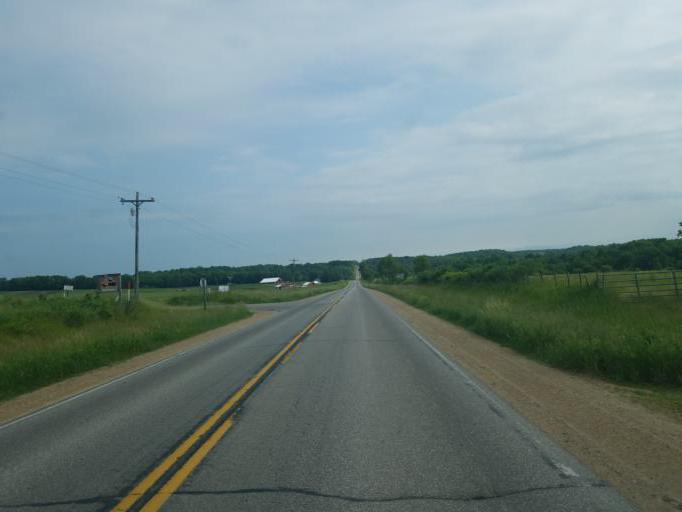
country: US
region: Wisconsin
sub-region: Vernon County
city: Hillsboro
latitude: 43.6251
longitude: -90.4525
